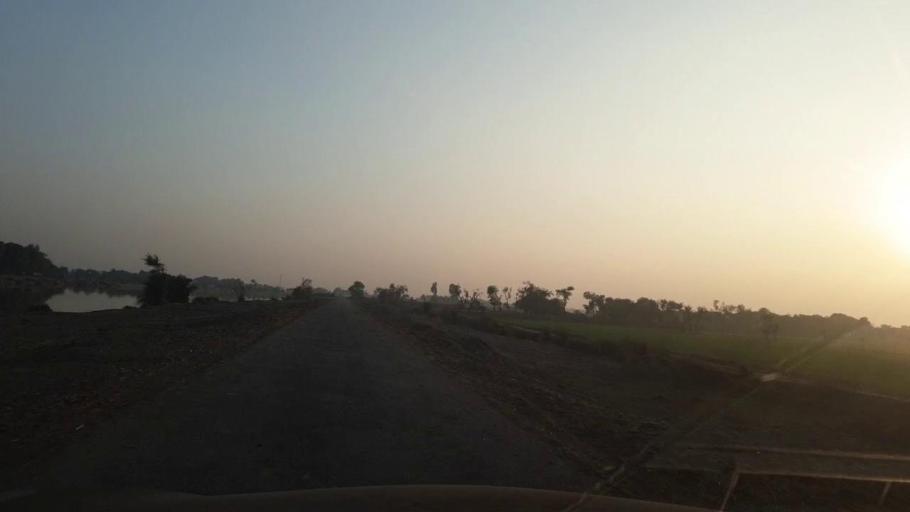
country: PK
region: Sindh
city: Ubauro
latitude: 28.2686
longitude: 69.7794
